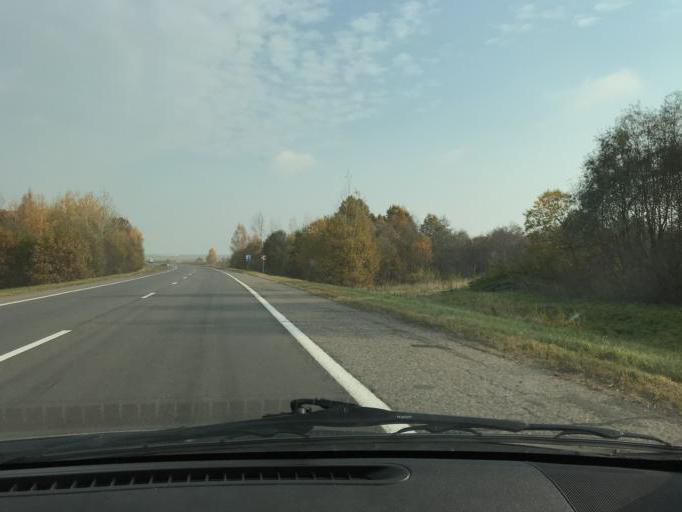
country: BY
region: Vitebsk
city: Chashniki
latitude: 54.9966
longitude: 28.9509
